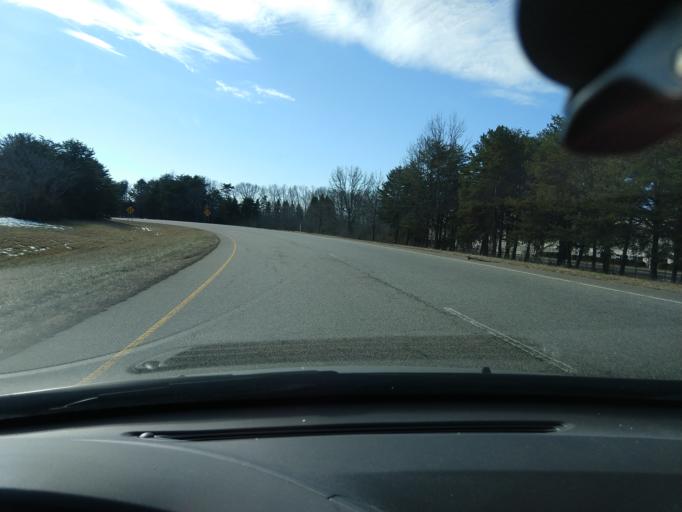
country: US
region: North Carolina
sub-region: Guilford County
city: Oak Ridge
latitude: 36.1079
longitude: -79.9665
